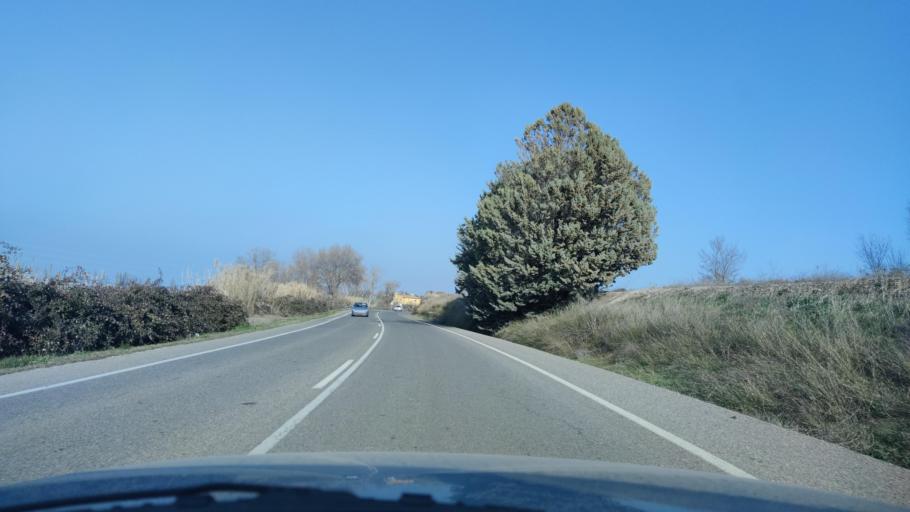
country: ES
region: Catalonia
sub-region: Provincia de Lleida
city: Lleida
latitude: 41.5769
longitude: 0.6121
